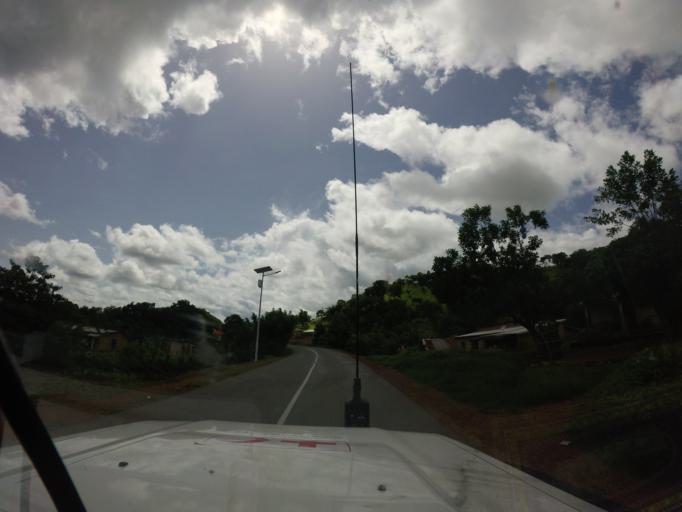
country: SL
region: Northern Province
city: Bindi
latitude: 10.1401
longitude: -11.6662
